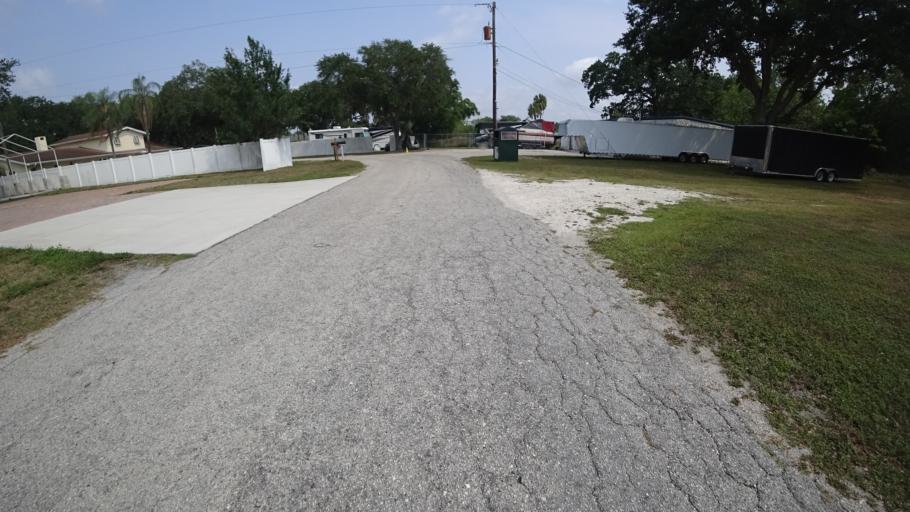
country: US
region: Florida
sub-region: Manatee County
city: Samoset
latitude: 27.4466
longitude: -82.5070
